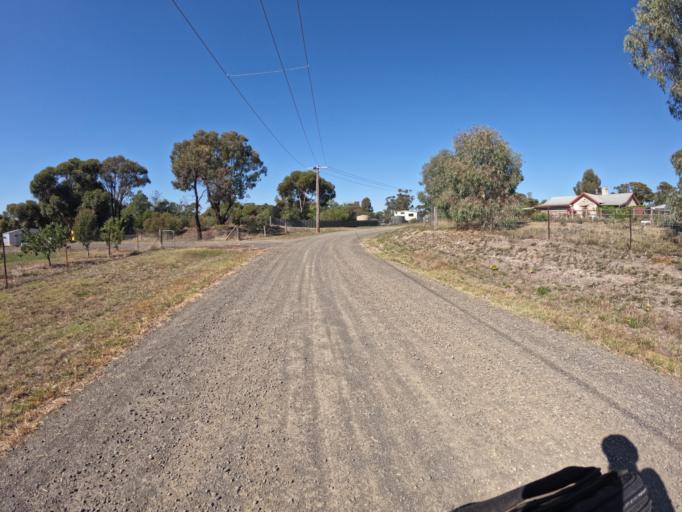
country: AU
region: Victoria
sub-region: Greater Bendigo
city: Kennington
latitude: -36.8261
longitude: 144.5847
